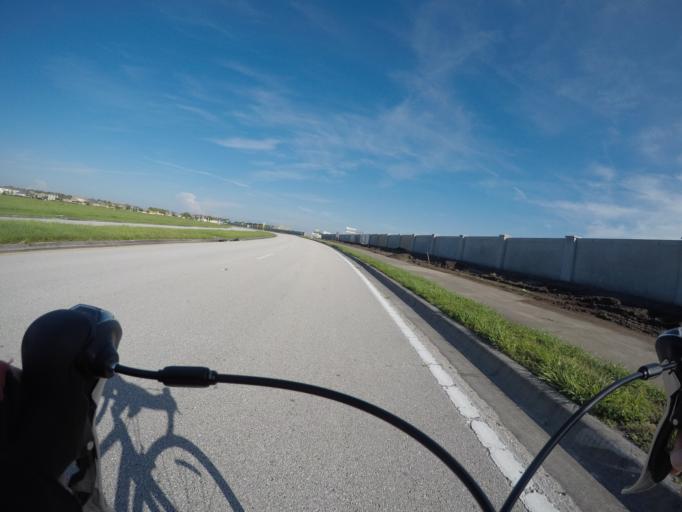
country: US
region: Florida
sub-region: Osceola County
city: Buenaventura Lakes
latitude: 28.3654
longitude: -81.3224
